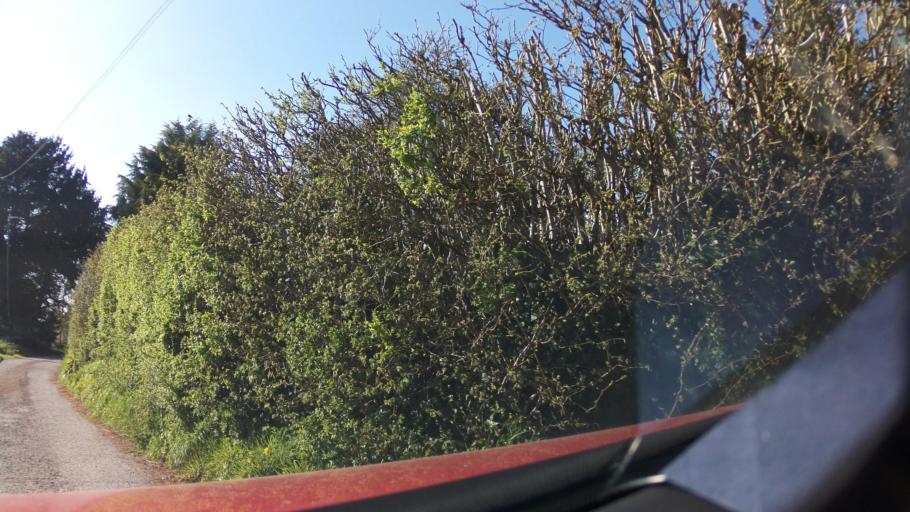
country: GB
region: England
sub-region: South Gloucestershire
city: Thornbury
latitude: 51.6329
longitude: -2.5690
